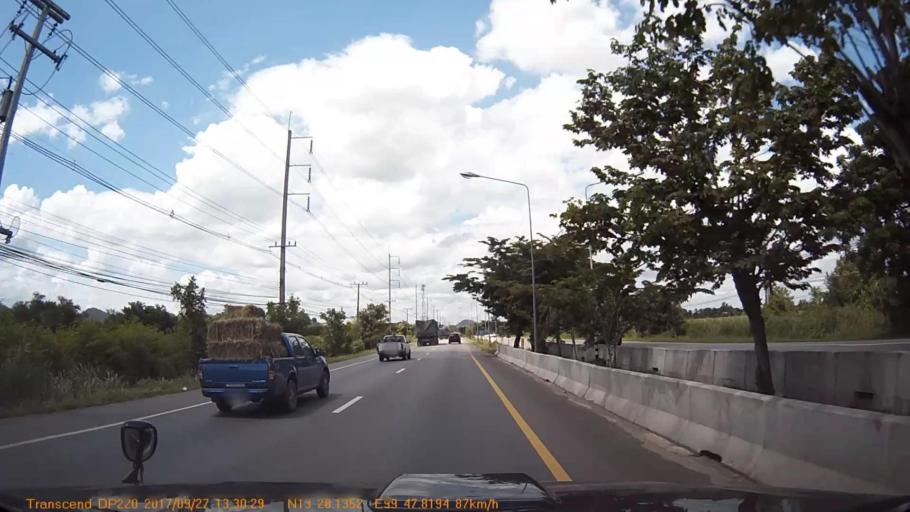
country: TH
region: Ratchaburi
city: Ratchaburi
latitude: 13.4689
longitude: 99.7970
